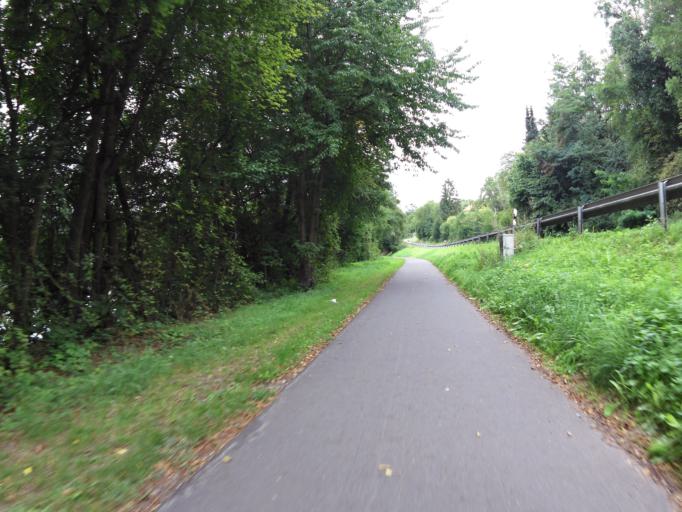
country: DE
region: Bavaria
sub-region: Regierungsbezirk Unterfranken
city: Eltmann
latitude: 49.9751
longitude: 10.6516
